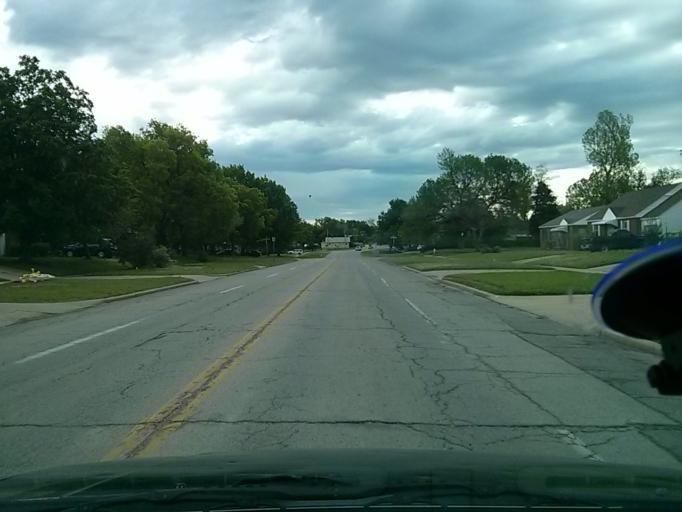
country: US
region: Oklahoma
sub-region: Tulsa County
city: Tulsa
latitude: 36.1566
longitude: -95.9526
